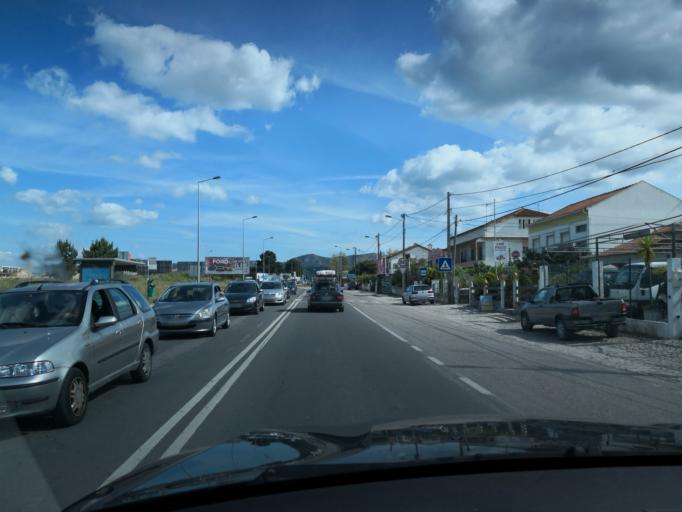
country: PT
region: Setubal
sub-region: Palmela
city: Quinta do Anjo
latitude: 38.5363
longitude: -9.0242
